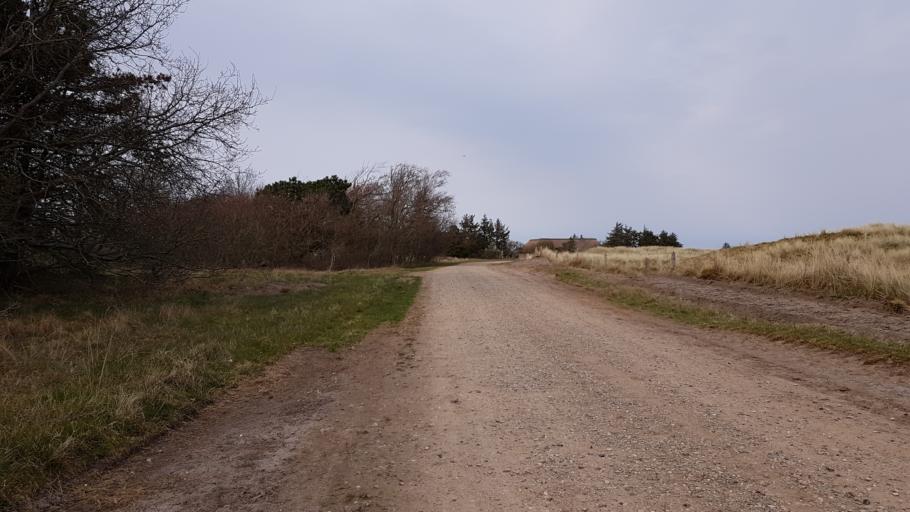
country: DE
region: Schleswig-Holstein
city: List
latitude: 55.1700
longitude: 8.5513
